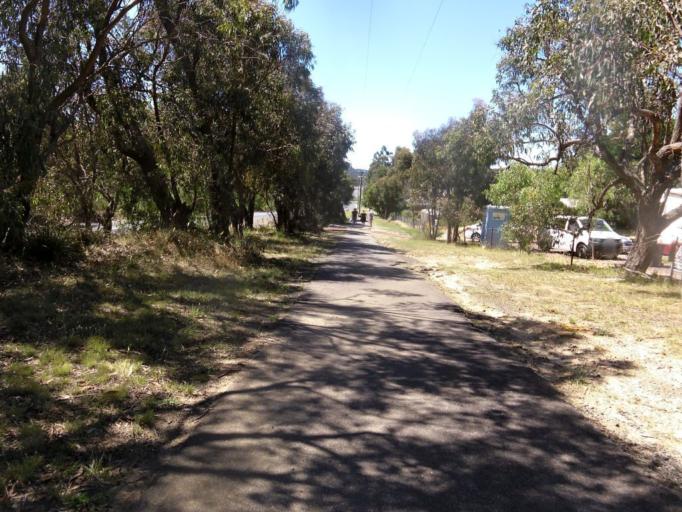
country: AU
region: Victoria
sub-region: Whittlesea
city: Whittlesea
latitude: -37.3658
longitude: 145.0267
